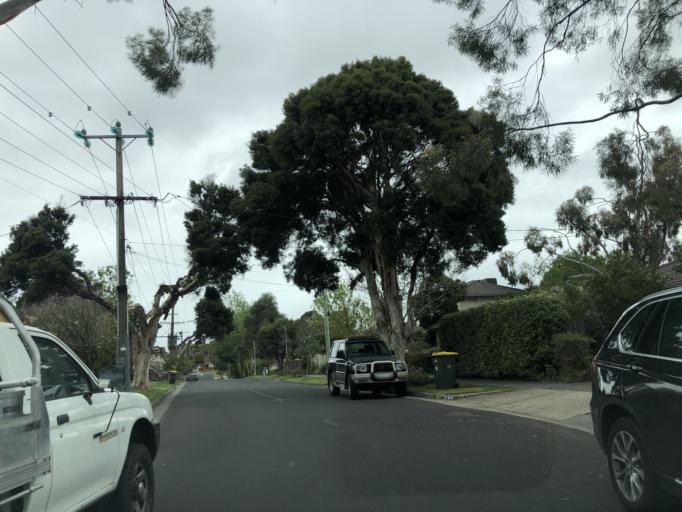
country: AU
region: Victoria
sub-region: Whitehorse
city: Blackburn South
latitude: -37.8375
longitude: 145.1443
